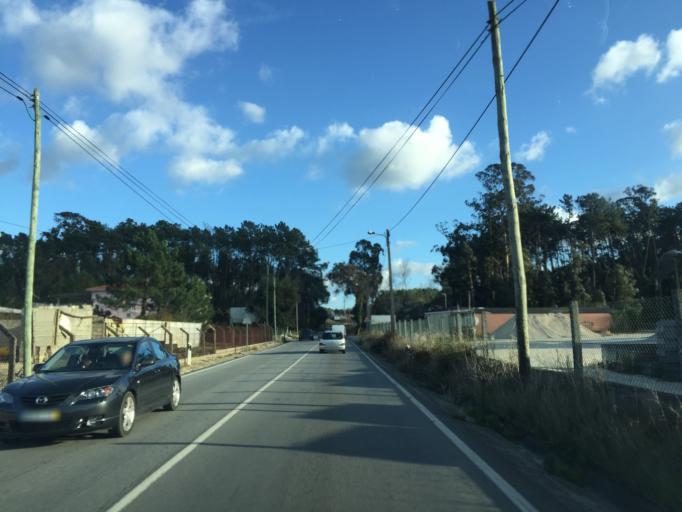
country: PT
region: Leiria
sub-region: Leiria
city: Souto da Carpalhosa
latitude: 39.8610
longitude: -8.8377
